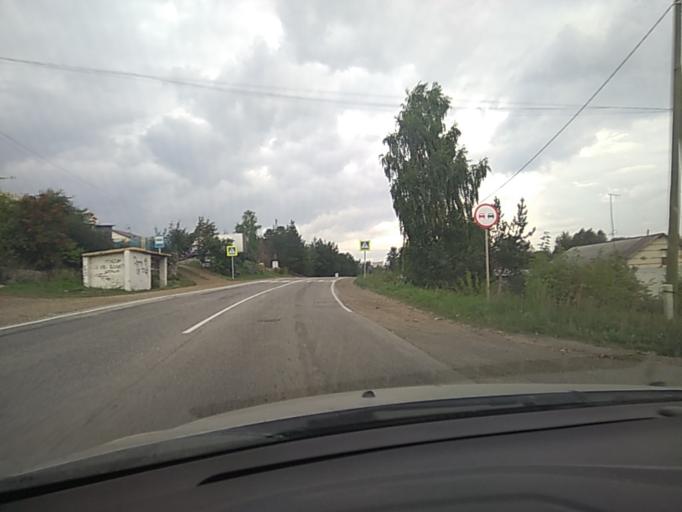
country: RU
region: Chelyabinsk
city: Kyshtym
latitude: 55.7216
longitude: 60.5114
